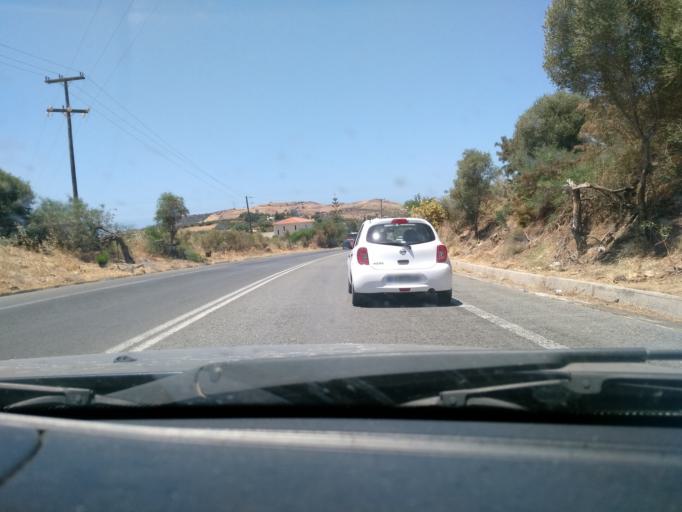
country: GR
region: Crete
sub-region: Nomos Rethymnis
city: Panormos
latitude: 35.4090
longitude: 24.7236
